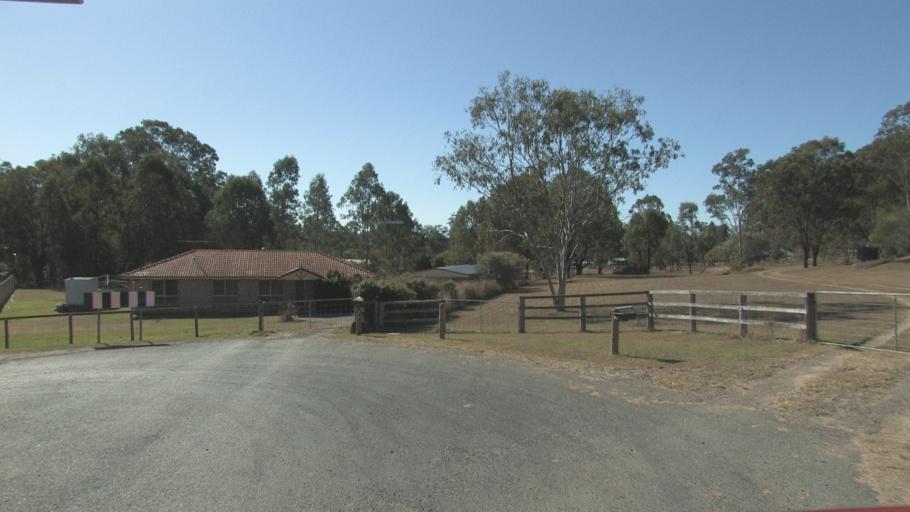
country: AU
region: Queensland
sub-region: Logan
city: Cedar Vale
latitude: -27.8562
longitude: 153.0348
